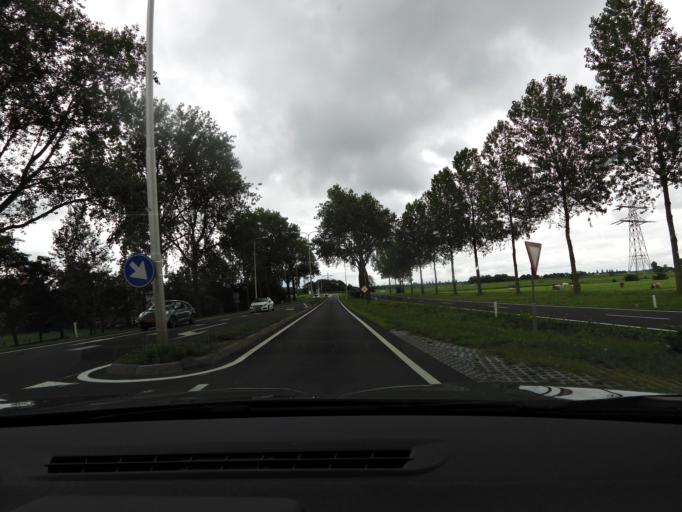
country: NL
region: South Holland
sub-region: Gemeente Maassluis
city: Maassluis
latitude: 51.8652
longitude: 4.2274
